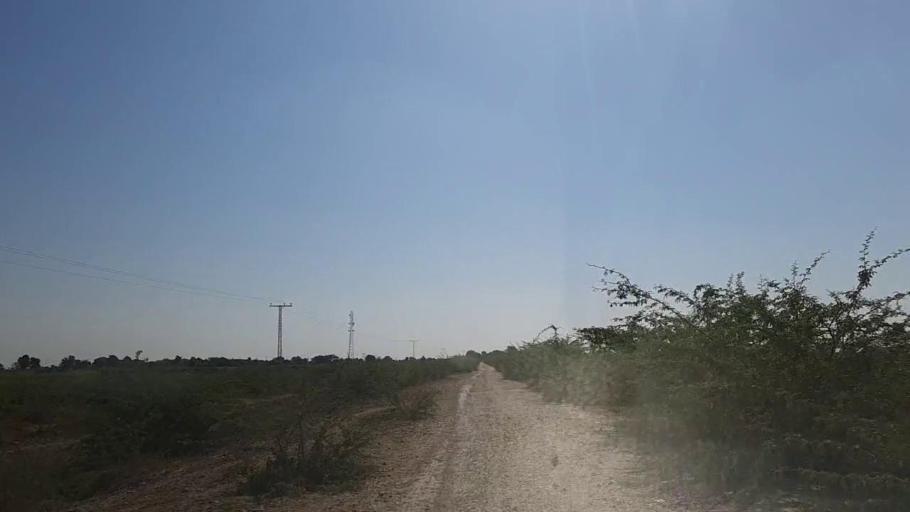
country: PK
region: Sindh
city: Naukot
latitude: 25.0074
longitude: 69.3762
